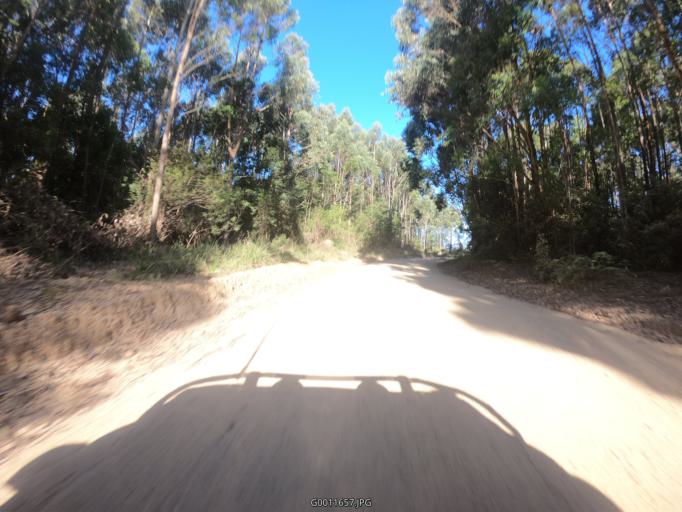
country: AU
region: New South Wales
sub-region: Lake Macquarie Shire
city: Cooranbong
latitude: -33.0482
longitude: 151.3151
